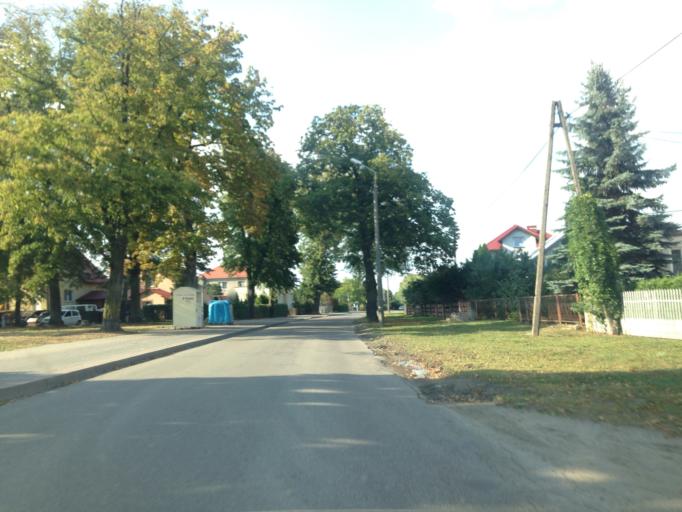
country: PL
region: Warmian-Masurian Voivodeship
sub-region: Powiat ilawski
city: Ilawa
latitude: 53.6154
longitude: 19.5682
